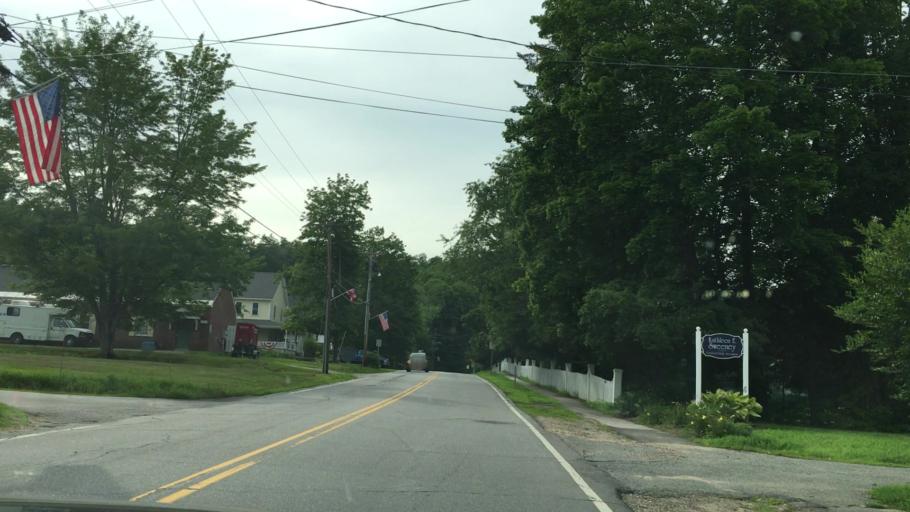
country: US
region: New Hampshire
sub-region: Carroll County
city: Center Harbor
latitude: 43.7093
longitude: -71.4637
